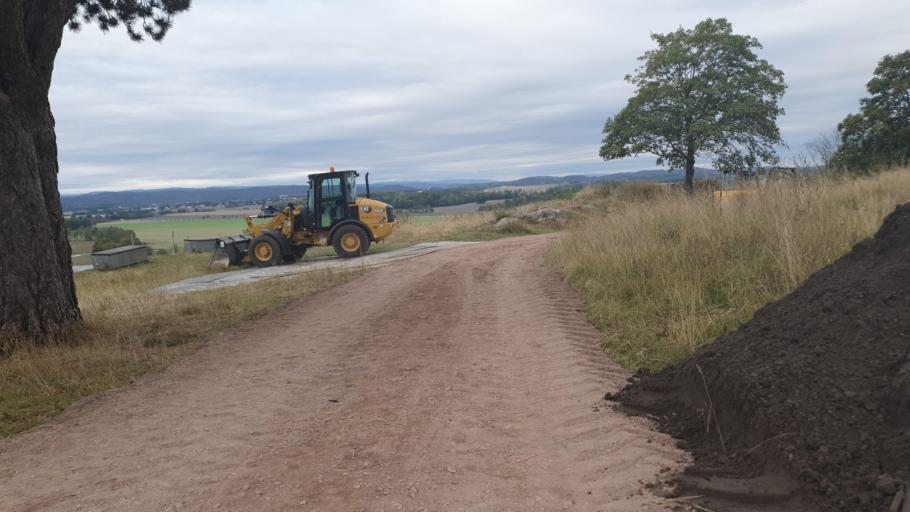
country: NO
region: Vestfold
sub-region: Tonsberg
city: Tonsberg
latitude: 59.2729
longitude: 10.4028
